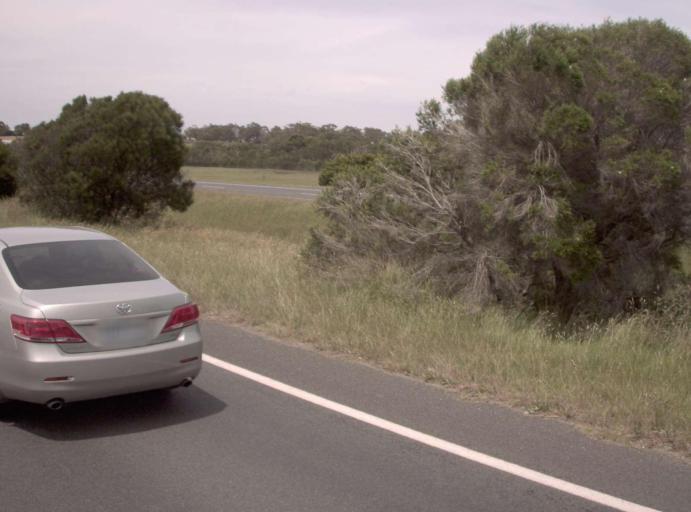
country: AU
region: Victoria
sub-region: Mornington Peninsula
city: Safety Beach
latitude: -38.3181
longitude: 145.0105
